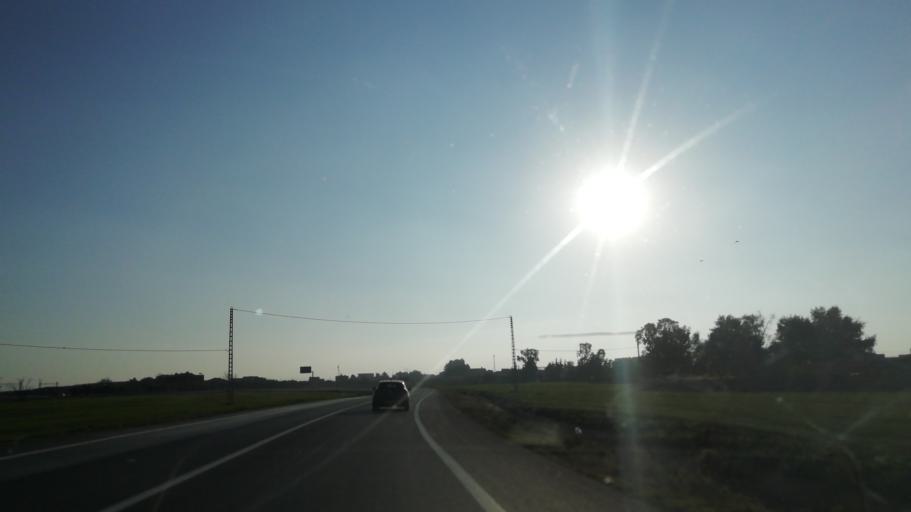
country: DZ
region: Sidi Bel Abbes
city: Sidi Bel Abbes
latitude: 35.1714
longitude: -0.6864
